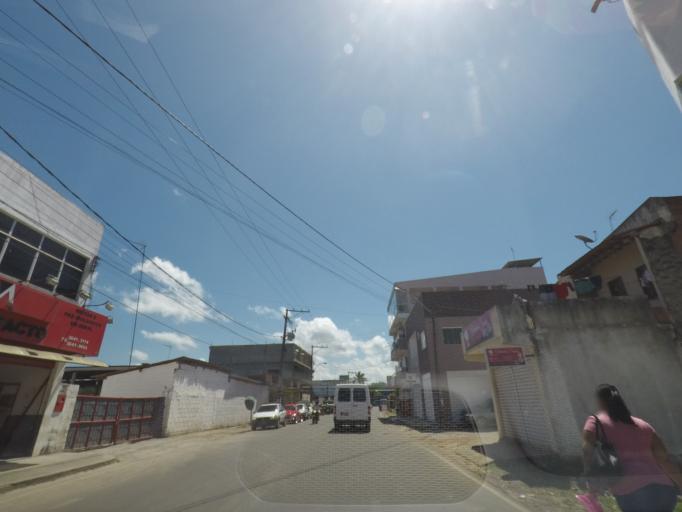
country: BR
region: Bahia
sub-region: Valenca
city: Valenca
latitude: -13.3756
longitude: -39.0737
